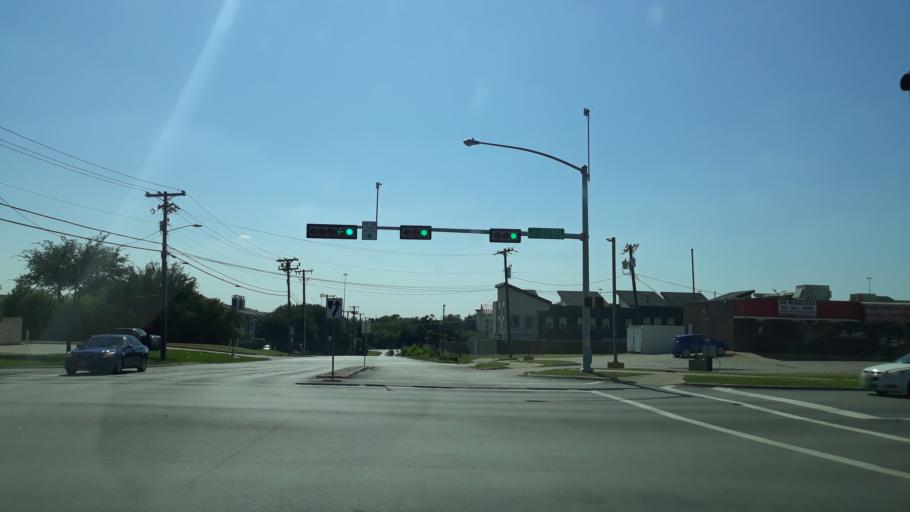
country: US
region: Texas
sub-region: Dallas County
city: Irving
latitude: 32.8332
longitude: -97.0094
